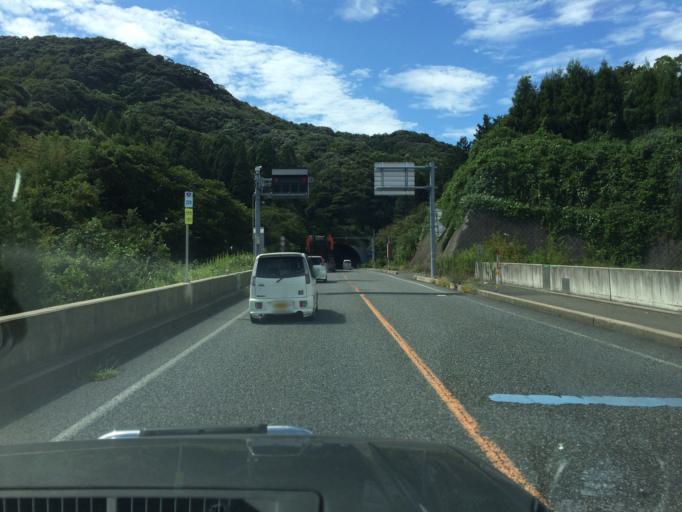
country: JP
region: Tottori
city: Tottori
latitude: 35.5149
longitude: 134.0215
